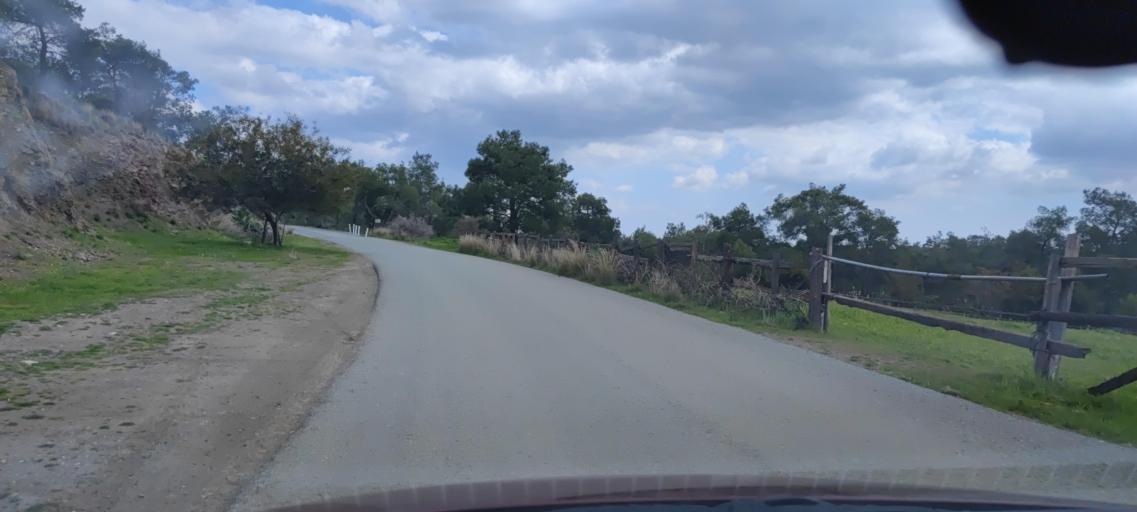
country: CY
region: Lefkosia
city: Lythrodontas
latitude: 34.9384
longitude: 33.3172
